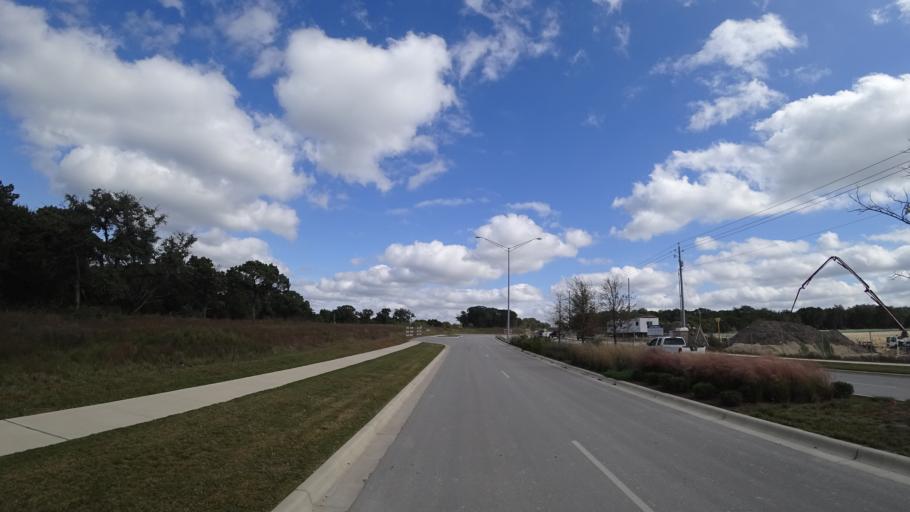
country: US
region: Texas
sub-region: Travis County
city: Barton Creek
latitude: 30.2616
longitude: -97.8572
